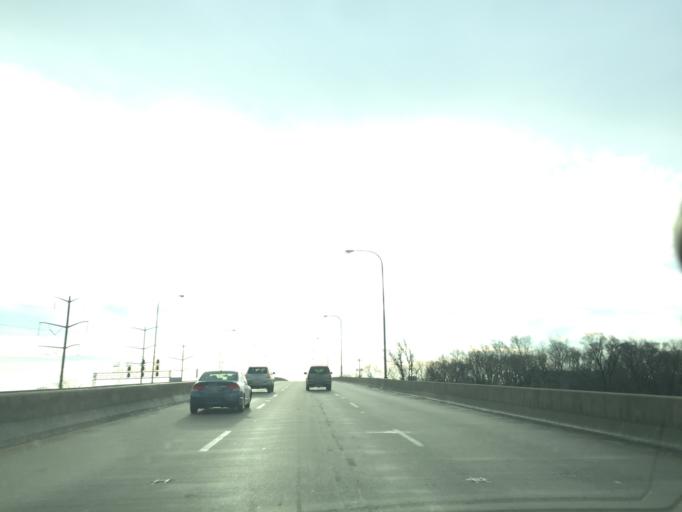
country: US
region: Illinois
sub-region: Cook County
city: Chicago
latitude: 41.7580
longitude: -87.5974
